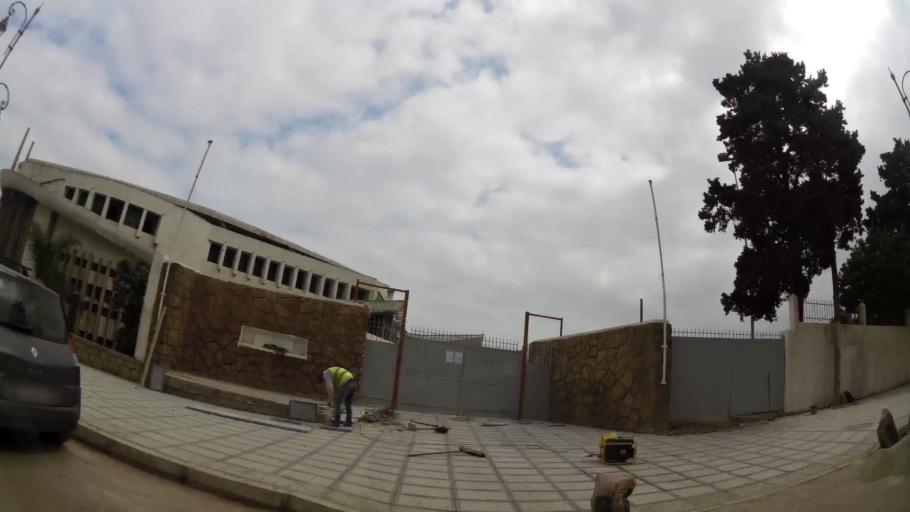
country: MA
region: Rabat-Sale-Zemmour-Zaer
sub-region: Rabat
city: Rabat
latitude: 34.0047
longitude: -6.8462
